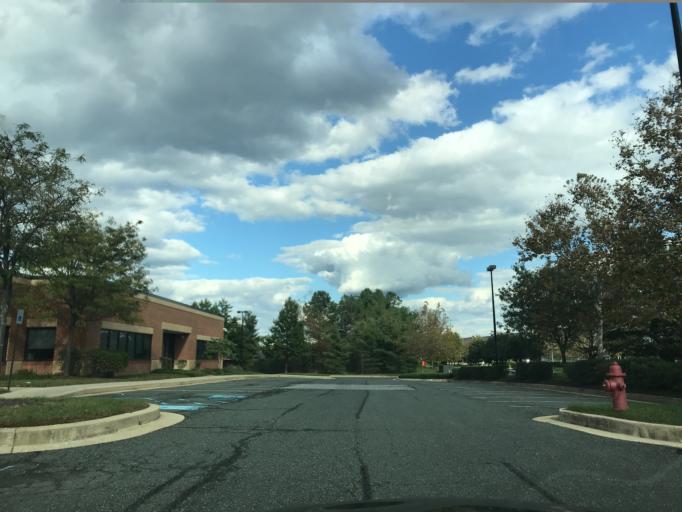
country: US
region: Maryland
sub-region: Baltimore County
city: White Marsh
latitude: 39.3672
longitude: -76.4595
